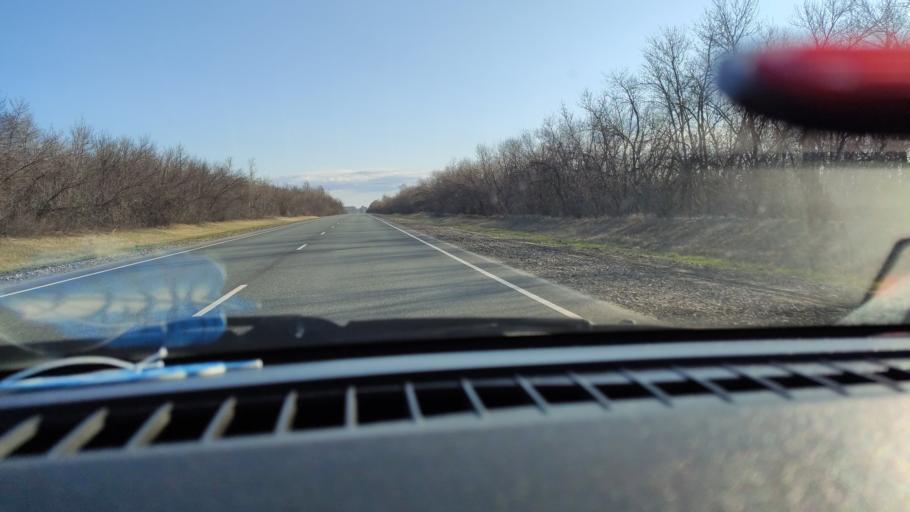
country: RU
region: Saratov
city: Khvalynsk
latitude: 52.5953
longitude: 48.1369
